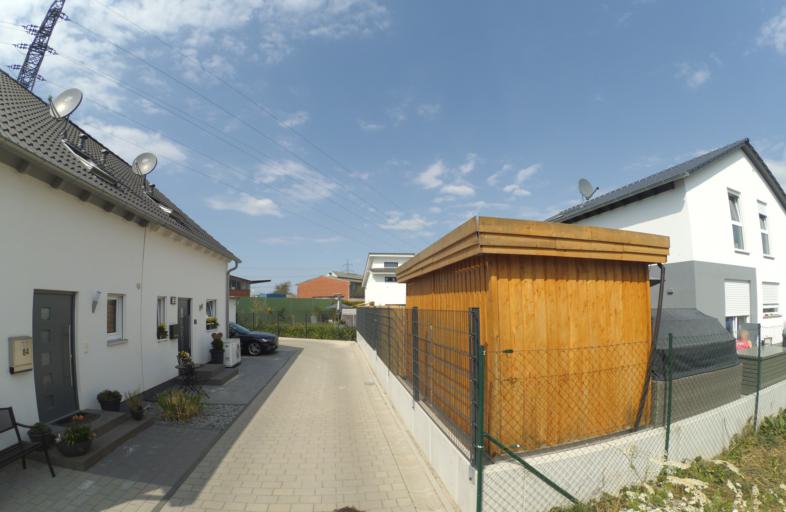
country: DE
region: Baden-Wuerttemberg
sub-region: Karlsruhe Region
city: Ladenburg
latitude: 49.4712
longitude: 8.5885
